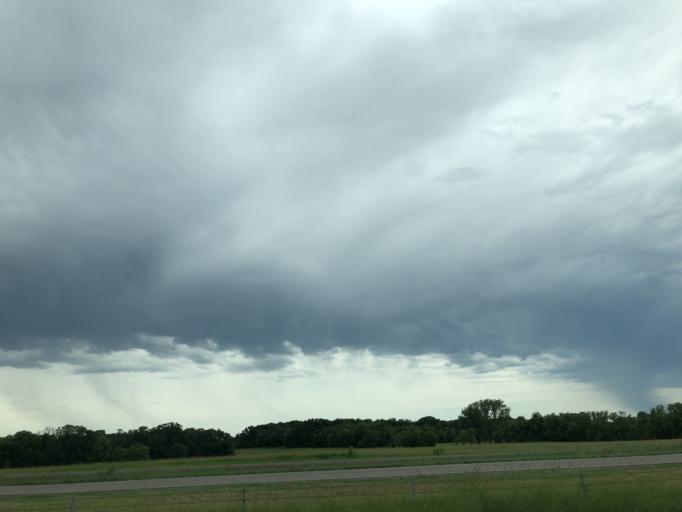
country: US
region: Minnesota
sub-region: Sherburne County
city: Becker
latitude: 45.3573
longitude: -93.9346
